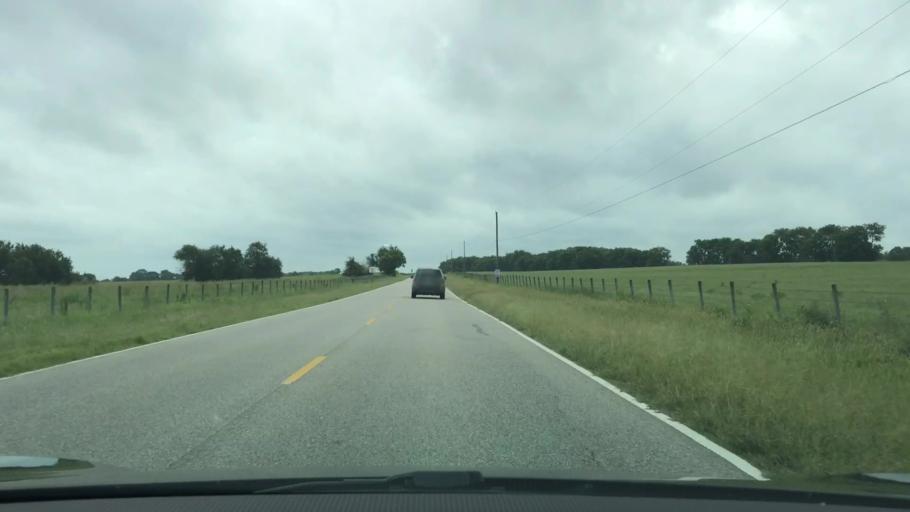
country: US
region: Alabama
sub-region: Montgomery County
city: Pike Road
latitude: 32.2833
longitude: -86.0989
